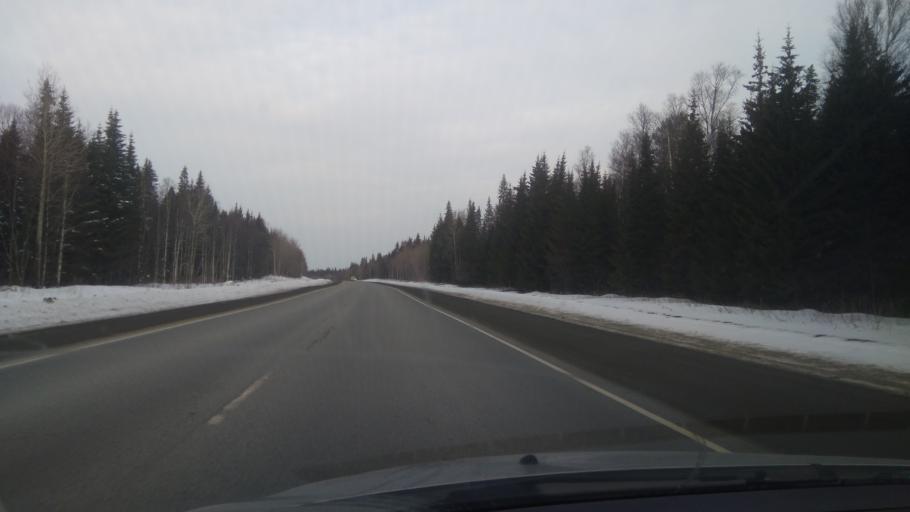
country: RU
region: Sverdlovsk
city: Atig
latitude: 56.8145
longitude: 59.3567
